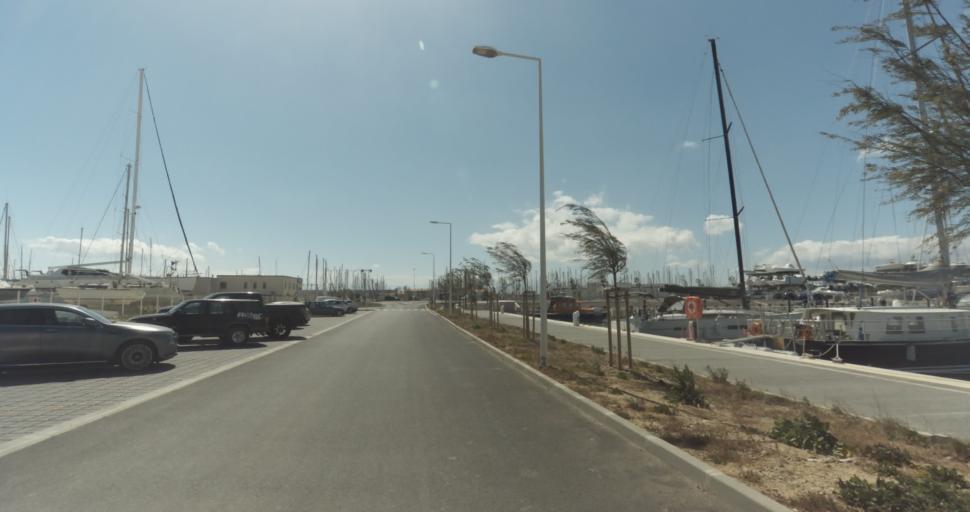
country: FR
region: Languedoc-Roussillon
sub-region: Departement de l'Aude
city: Leucate
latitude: 42.8675
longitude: 3.0423
